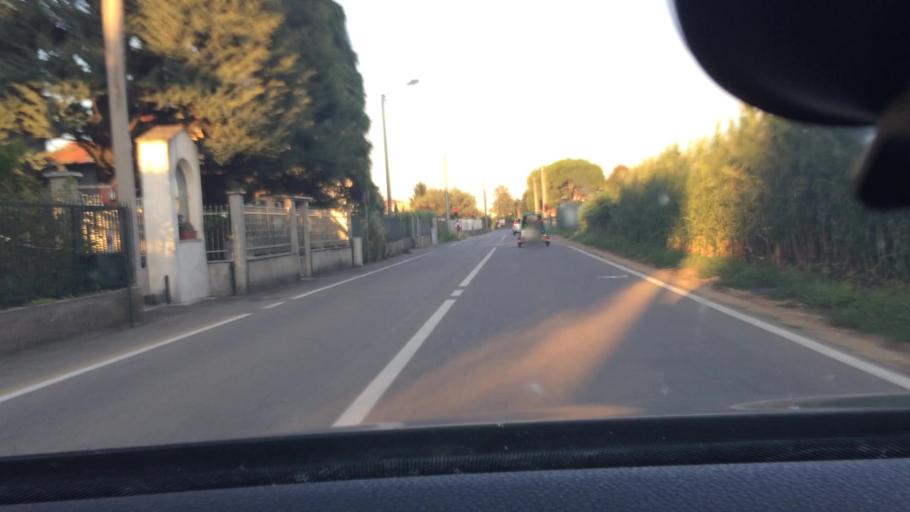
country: IT
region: Lombardy
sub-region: Provincia di Como
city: Turate
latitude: 45.6555
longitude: 9.0103
